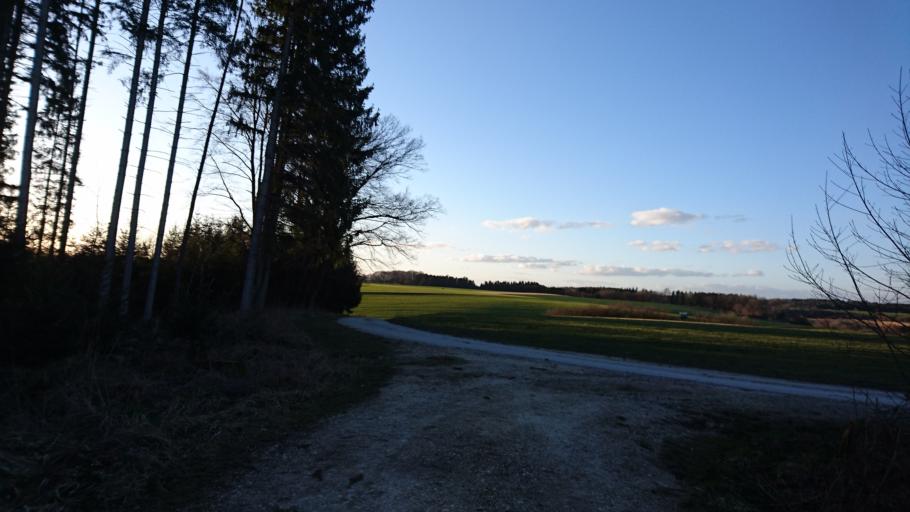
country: DE
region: Bavaria
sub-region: Swabia
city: Altenmunster
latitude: 48.4372
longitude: 10.6205
